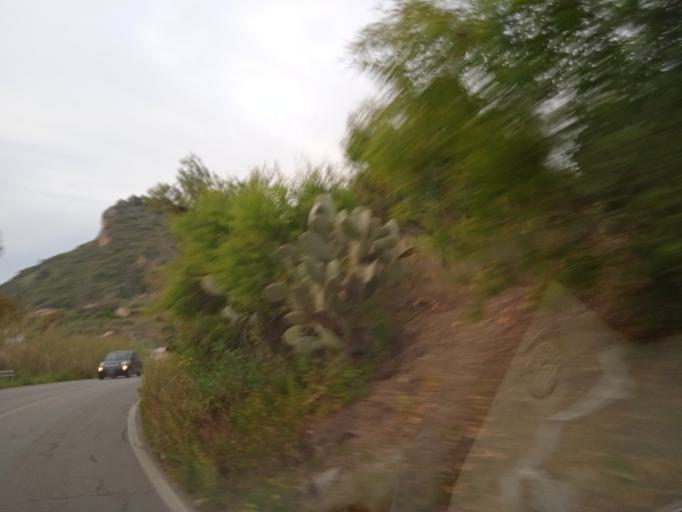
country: IT
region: Sicily
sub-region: Palermo
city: Portella di Mare
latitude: 38.0498
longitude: 13.4610
